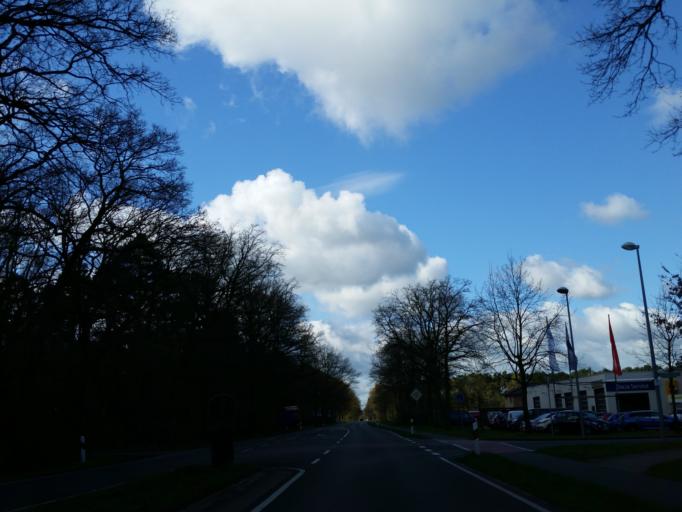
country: DE
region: Lower Saxony
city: Rotenburg
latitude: 53.0945
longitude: 9.3741
